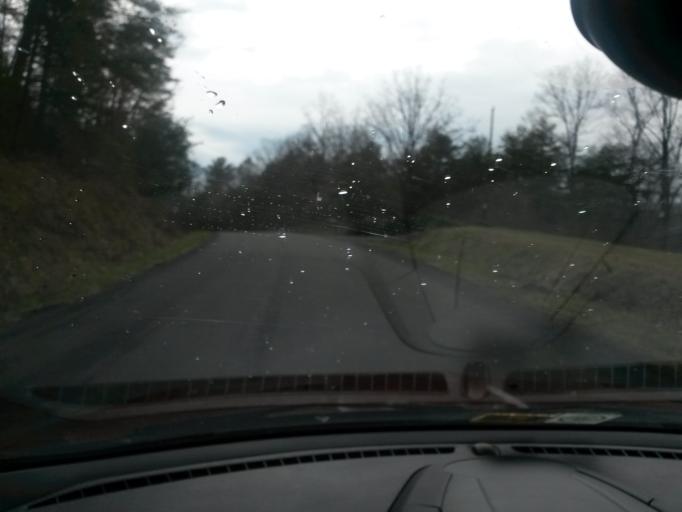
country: US
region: Virginia
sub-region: Bath County
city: Warm Springs
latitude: 38.0839
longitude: -79.8078
